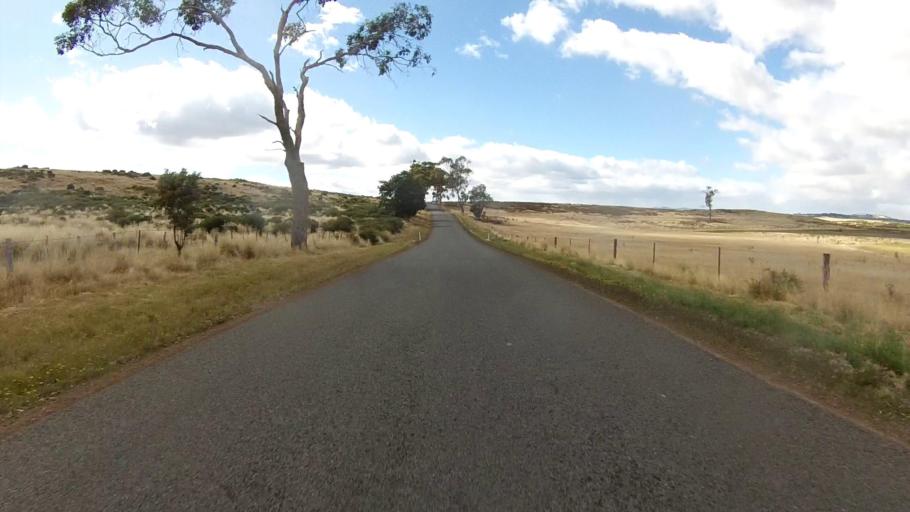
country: AU
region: Tasmania
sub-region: Northern Midlands
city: Evandale
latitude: -41.7045
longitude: 147.3878
